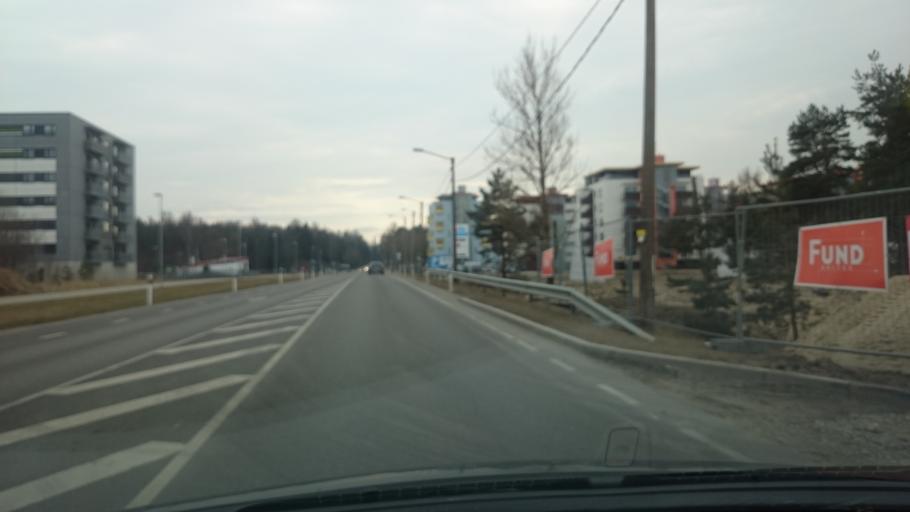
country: EE
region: Harju
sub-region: Saue vald
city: Laagri
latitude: 59.3963
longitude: 24.6447
